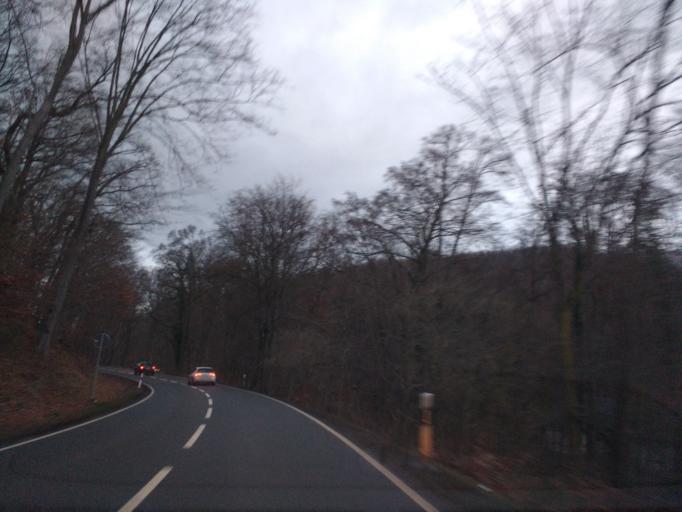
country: DE
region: Saxony-Anhalt
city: Bad Suderode
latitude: 51.7227
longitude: 11.1134
